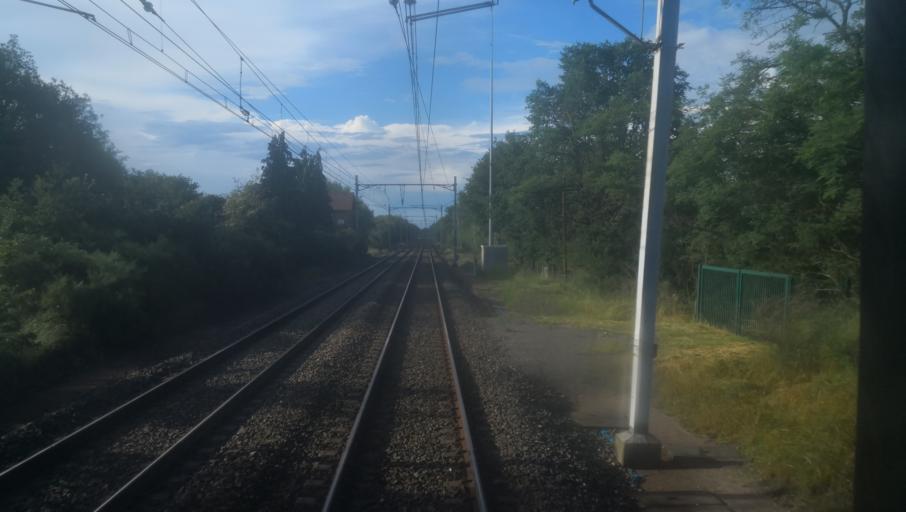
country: FR
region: Centre
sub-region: Departement du Loir-et-Cher
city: Salbris
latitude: 47.3870
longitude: 2.0507
